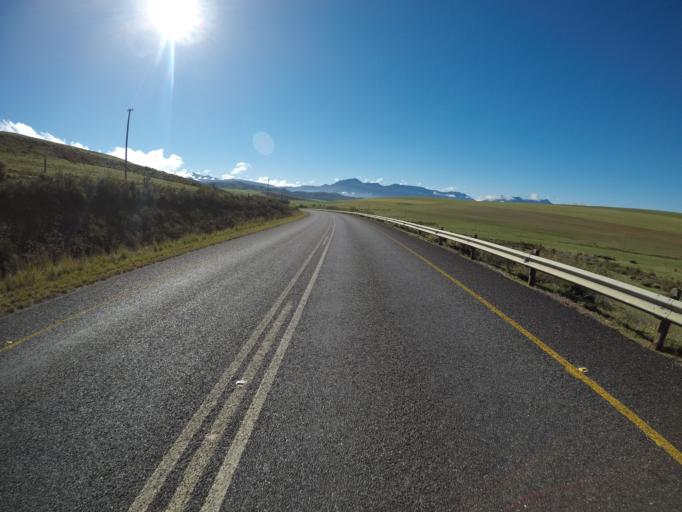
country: ZA
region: Western Cape
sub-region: Overberg District Municipality
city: Caledon
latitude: -34.1314
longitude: 19.5126
